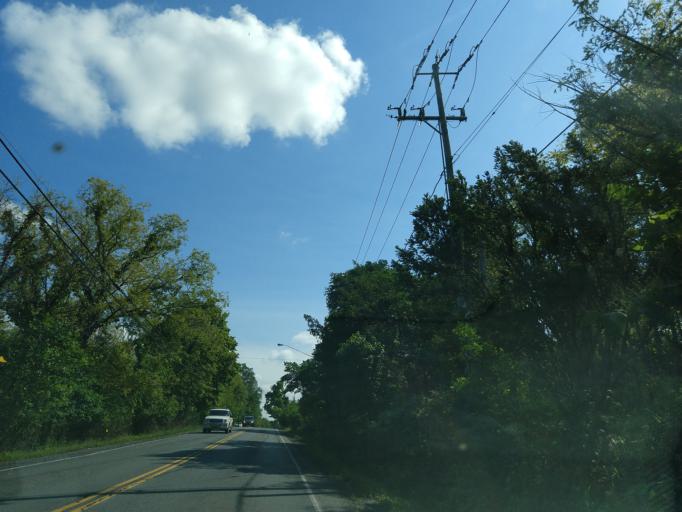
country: US
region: New York
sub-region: Tompkins County
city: South Hill
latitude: 42.4288
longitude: -76.4909
